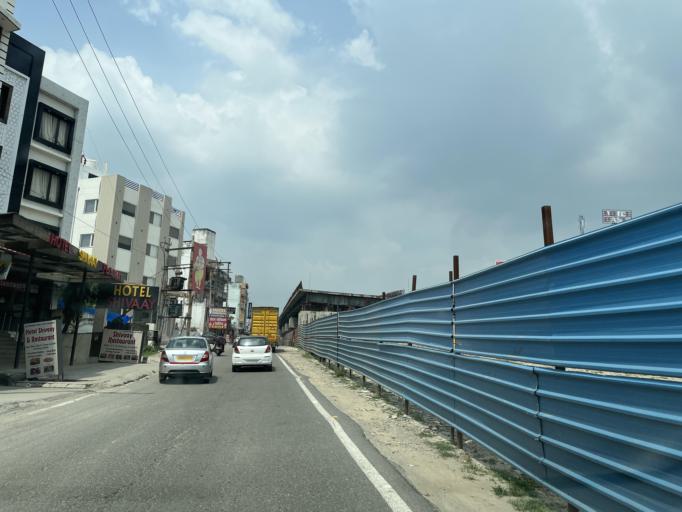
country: IN
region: Uttarakhand
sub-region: Haridwar
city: Haridwar
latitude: 29.9799
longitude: 78.1826
